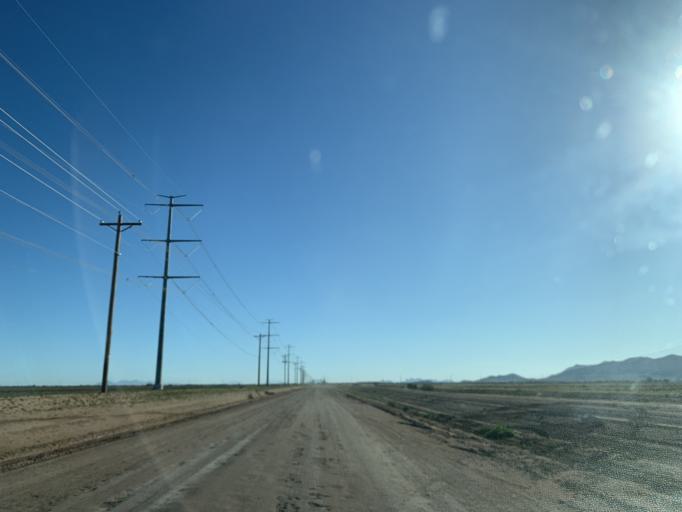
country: US
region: Arizona
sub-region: Pinal County
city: Casa Grande
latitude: 32.8612
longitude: -111.6709
